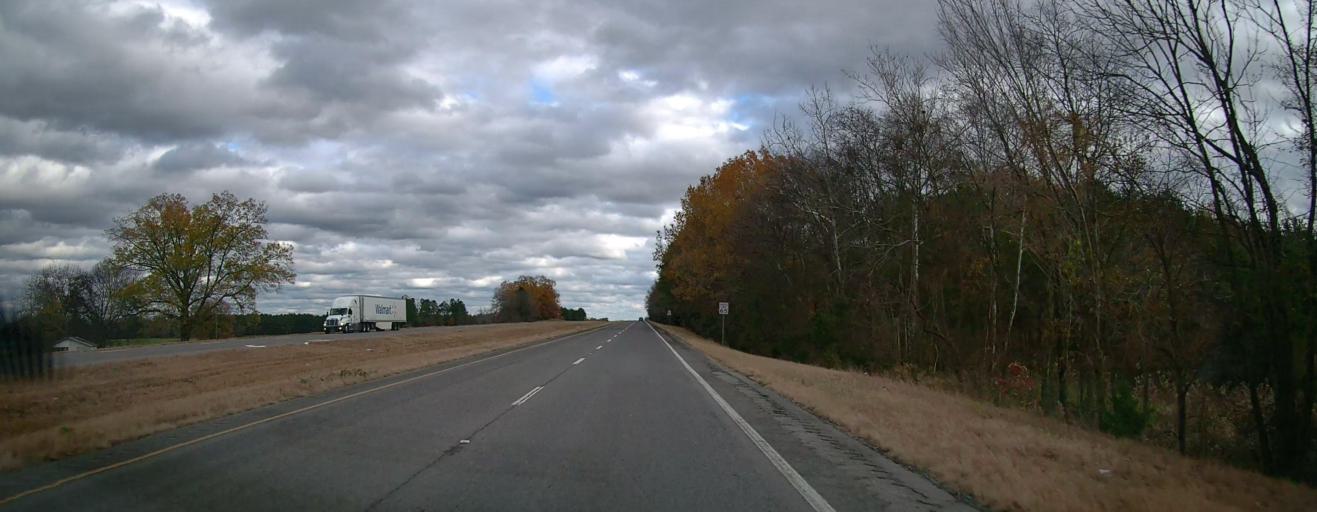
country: US
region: Alabama
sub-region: Morgan County
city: Danville
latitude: 34.3934
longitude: -87.1190
